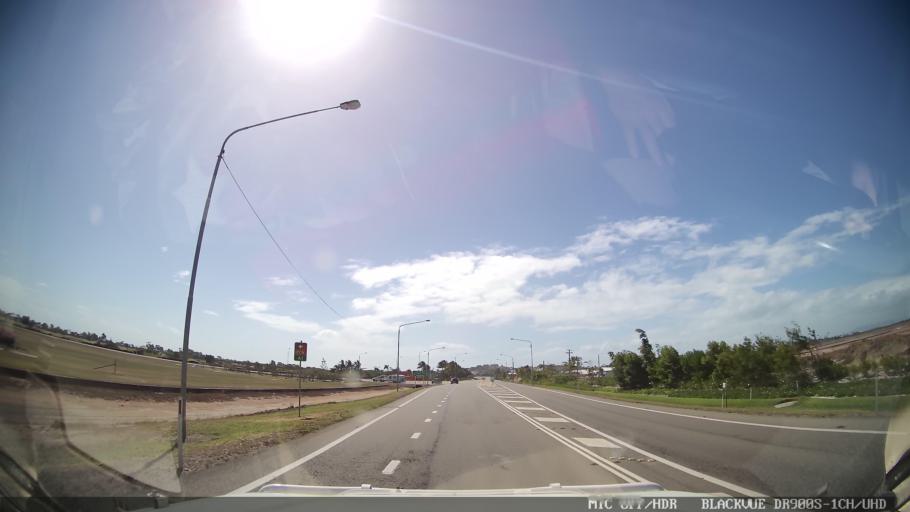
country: AU
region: Queensland
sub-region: Whitsunday
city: Bowen
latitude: -20.0160
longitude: 148.2203
